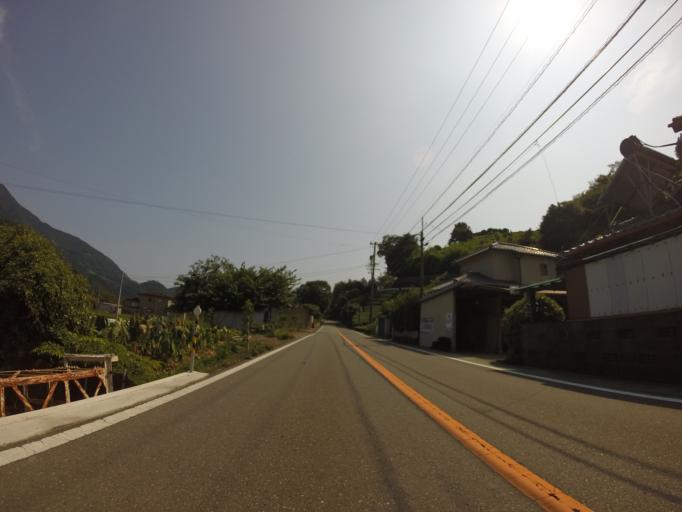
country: JP
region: Shizuoka
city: Shizuoka-shi
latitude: 35.0847
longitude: 138.3695
